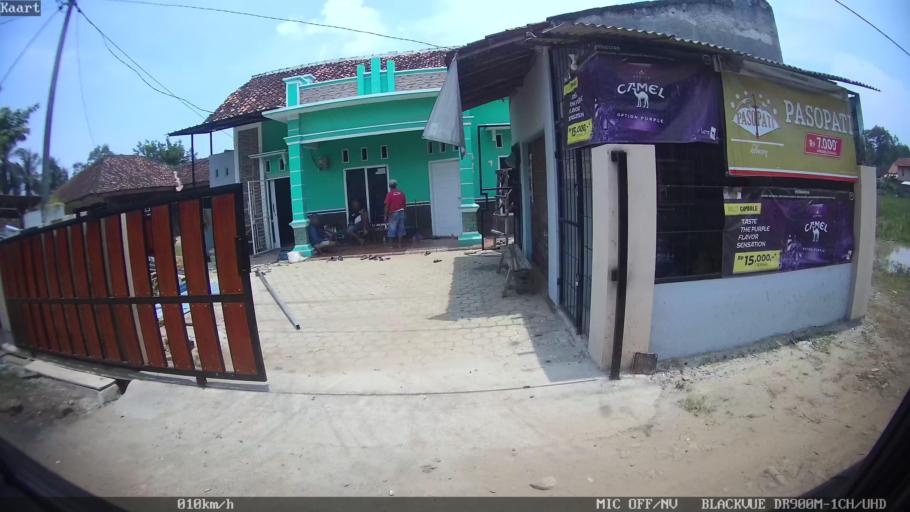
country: ID
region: Lampung
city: Natar
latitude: -5.3153
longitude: 105.2397
